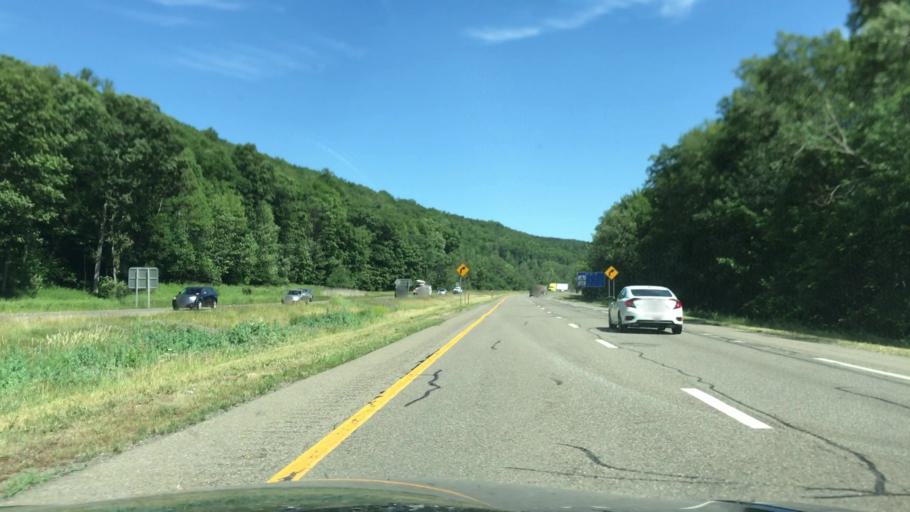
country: US
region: New York
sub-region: Steuben County
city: Painted Post
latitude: 42.1767
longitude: -77.1109
